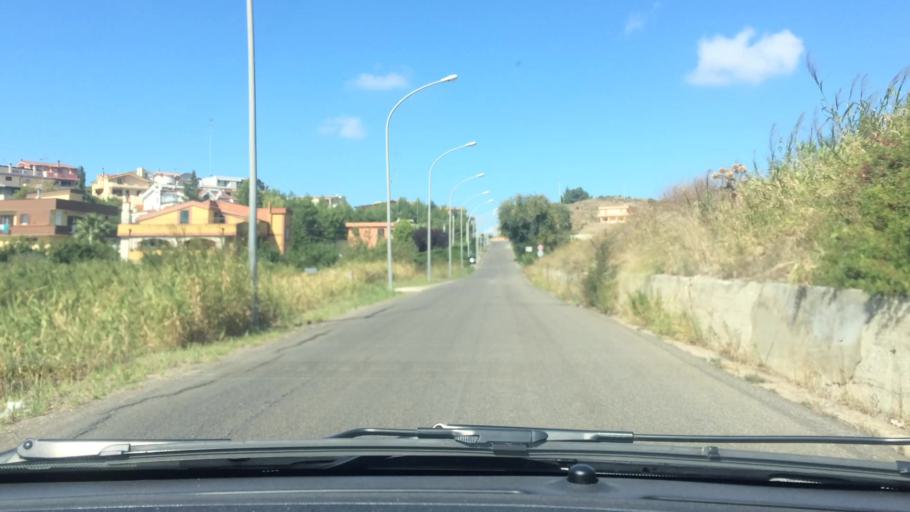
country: IT
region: Basilicate
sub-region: Provincia di Matera
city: Montescaglioso
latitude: 40.5427
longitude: 16.6716
